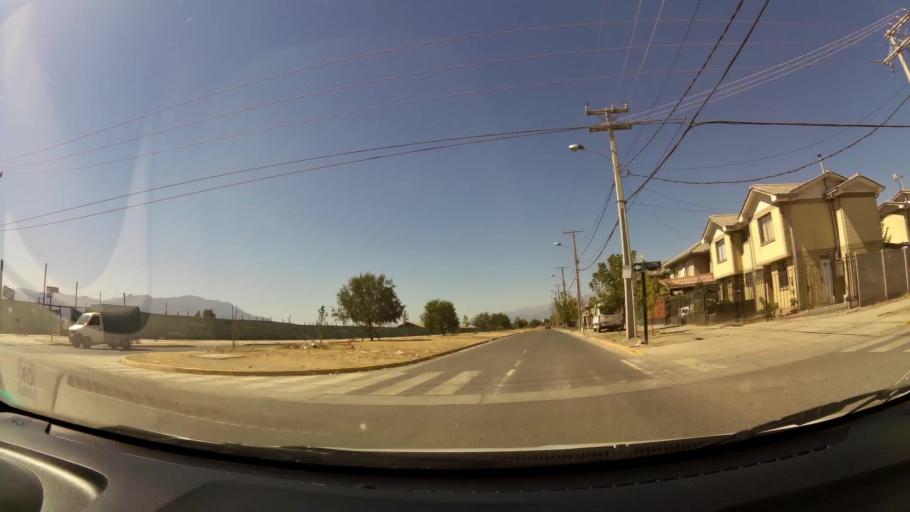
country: CL
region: O'Higgins
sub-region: Provincia de Cachapoal
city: Rancagua
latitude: -34.1753
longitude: -70.7719
